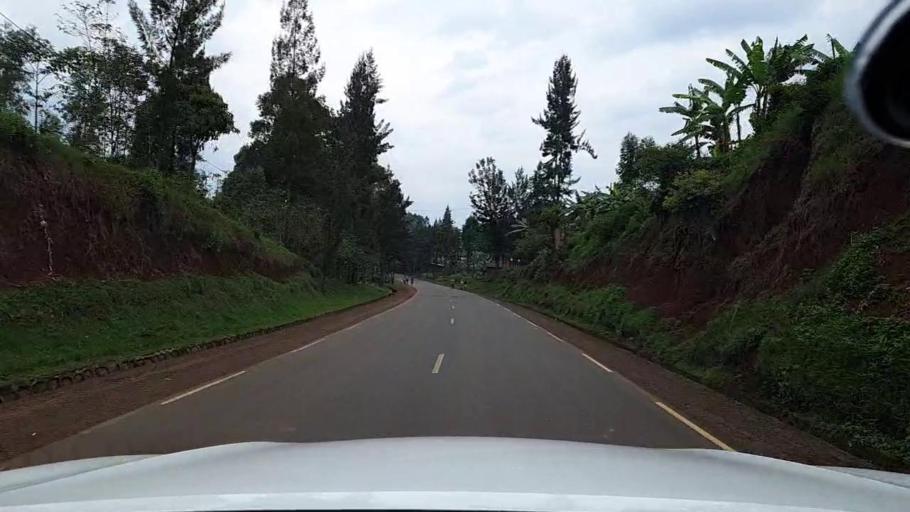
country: RW
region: Western Province
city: Cyangugu
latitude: -2.6107
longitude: 28.9367
